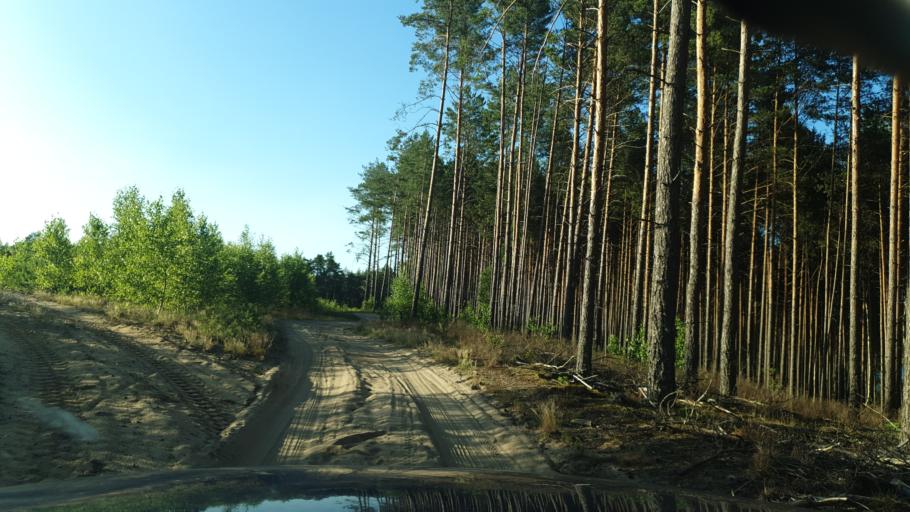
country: PL
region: Pomeranian Voivodeship
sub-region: Powiat bytowski
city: Lipnica
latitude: 53.8833
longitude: 17.4268
